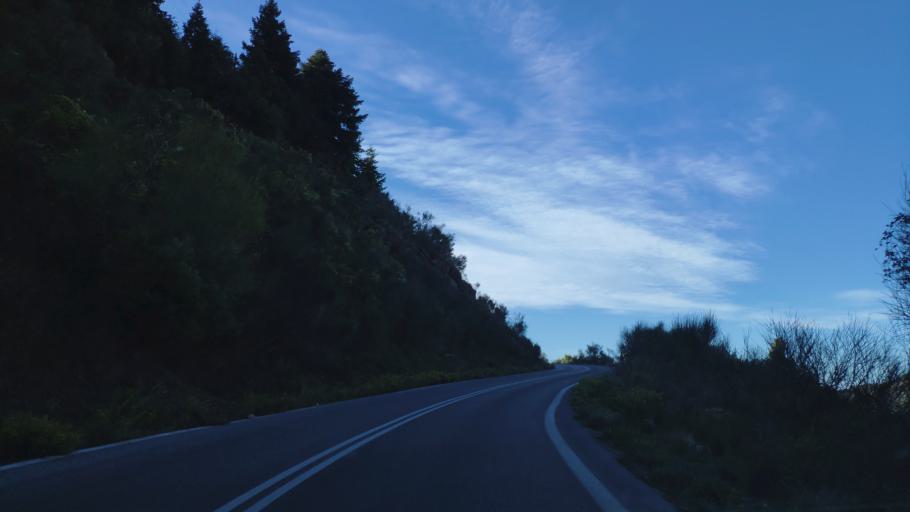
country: GR
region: Peloponnese
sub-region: Nomos Arkadias
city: Dimitsana
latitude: 37.5784
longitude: 22.0613
